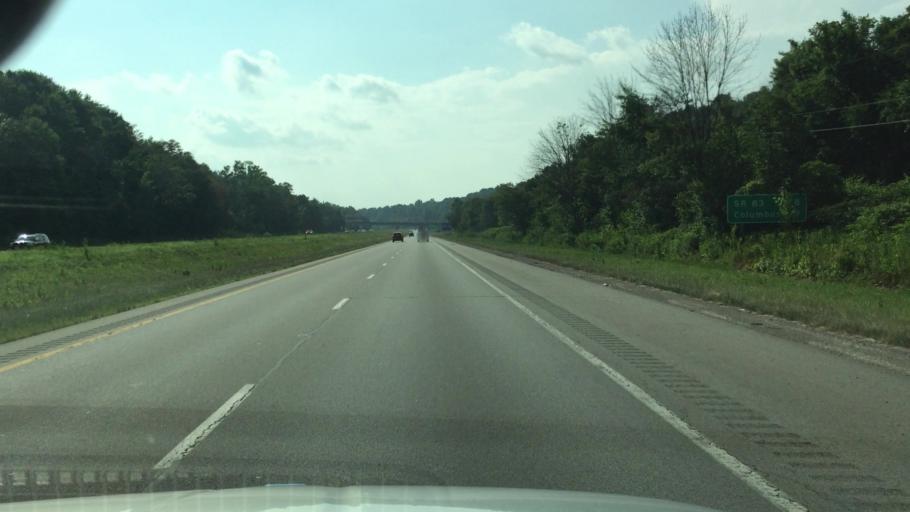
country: US
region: Ohio
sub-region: Guernsey County
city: Cambridge
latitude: 40.0042
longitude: -81.5940
